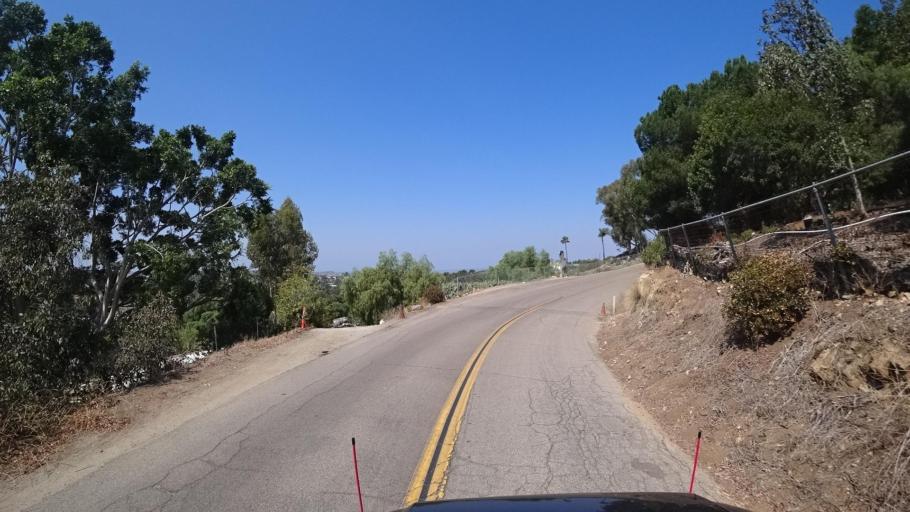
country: US
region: California
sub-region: San Diego County
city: Vista
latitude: 33.2414
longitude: -117.2324
